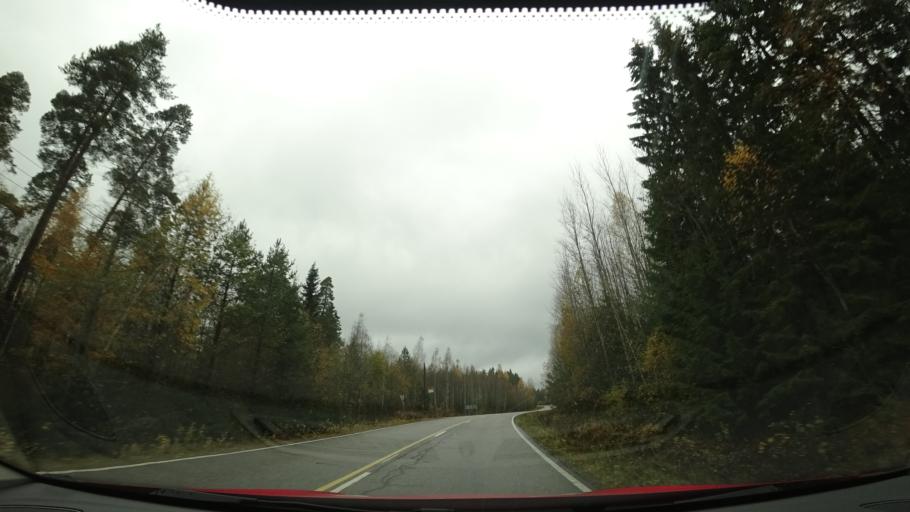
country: FI
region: Uusimaa
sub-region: Helsinki
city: Sibbo
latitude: 60.2816
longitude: 25.1962
